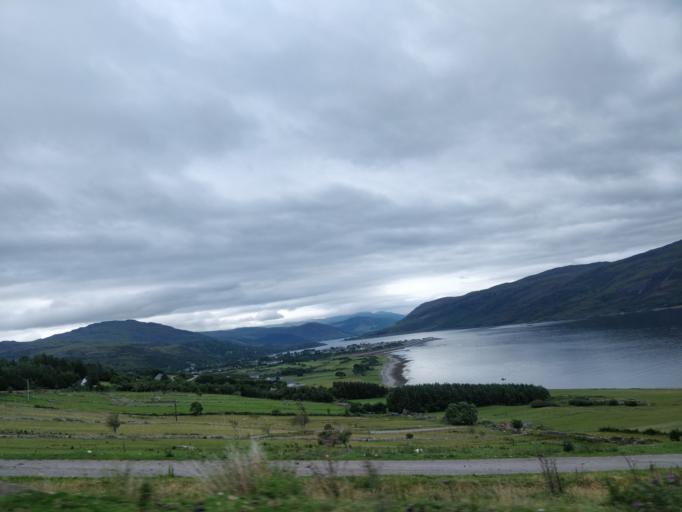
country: GB
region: Scotland
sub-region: Highland
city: Ullapool
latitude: 57.9126
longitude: -5.1871
